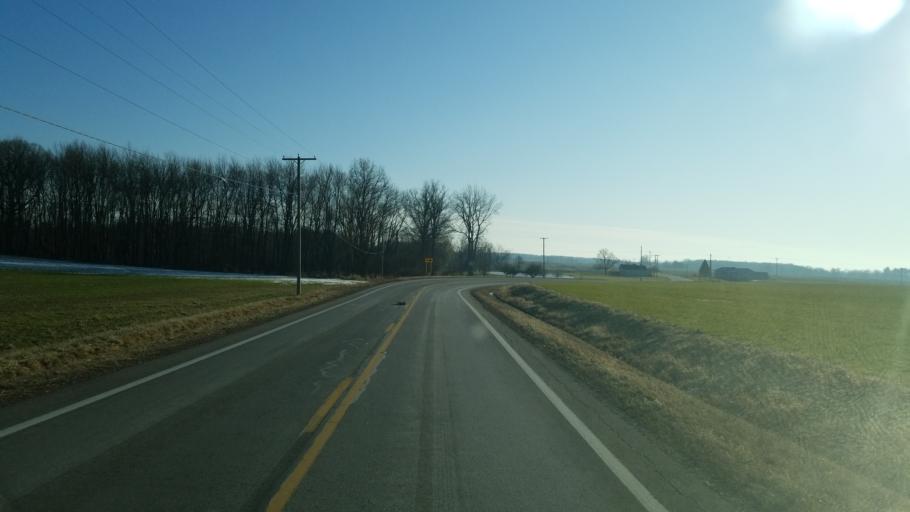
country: US
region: Ohio
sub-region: Seneca County
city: Tiffin
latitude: 41.0419
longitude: -83.0155
